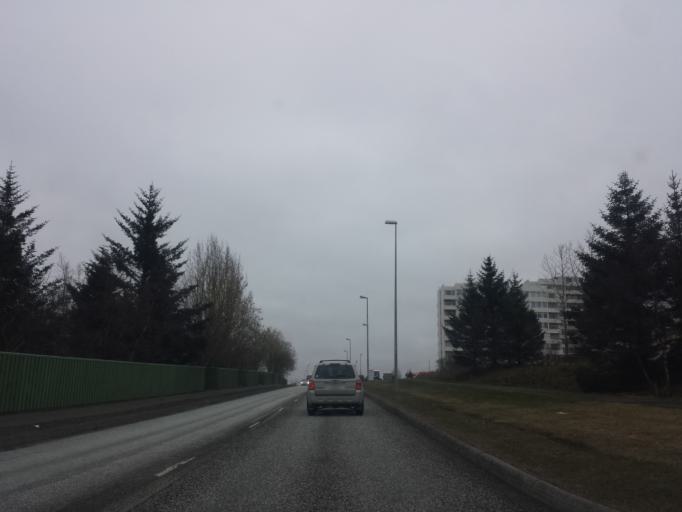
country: IS
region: Capital Region
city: Reykjavik
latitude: 64.1137
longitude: -21.8720
